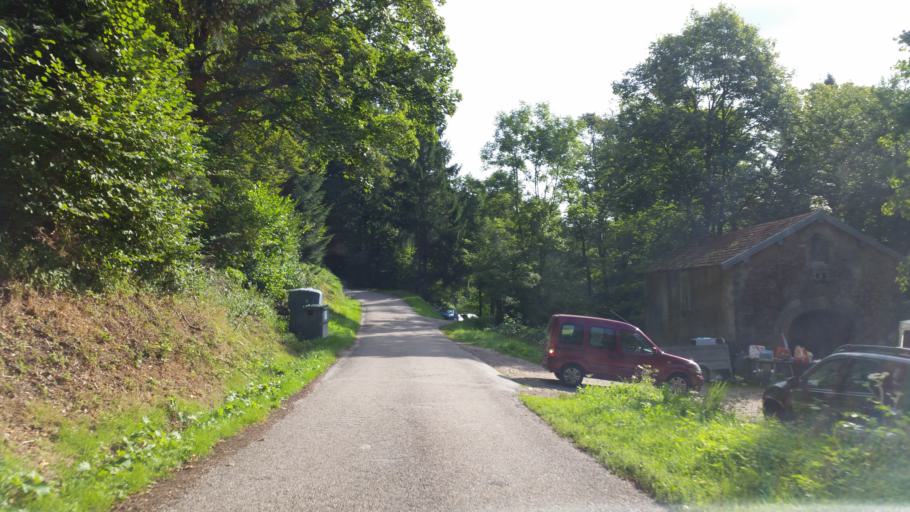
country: FR
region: Lorraine
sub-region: Departement des Vosges
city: Remiremont
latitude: 47.9613
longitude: 6.5798
